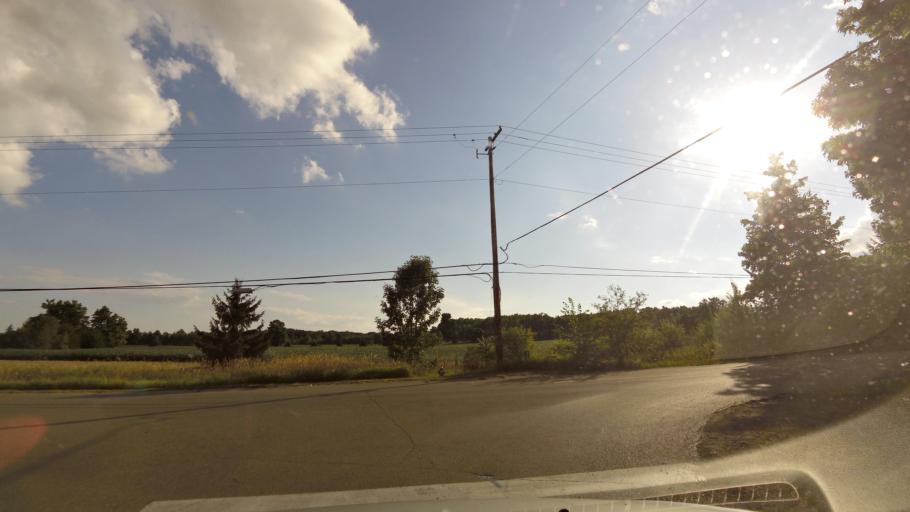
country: CA
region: Ontario
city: Brampton
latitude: 43.7590
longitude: -79.9308
